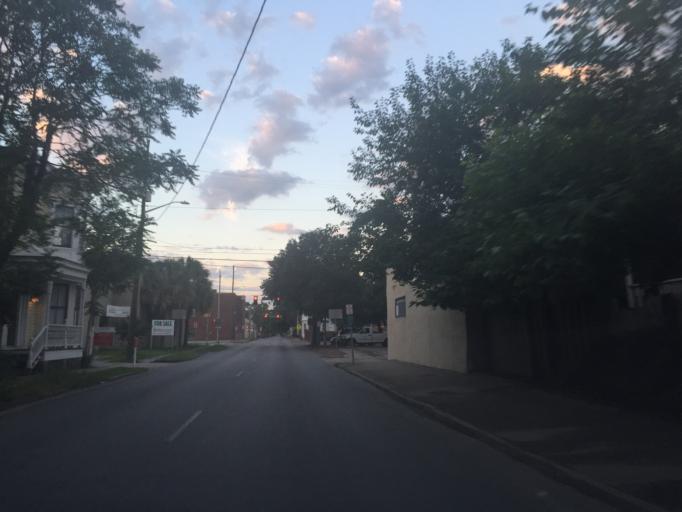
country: US
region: Georgia
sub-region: Chatham County
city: Savannah
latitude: 32.0643
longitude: -81.0987
